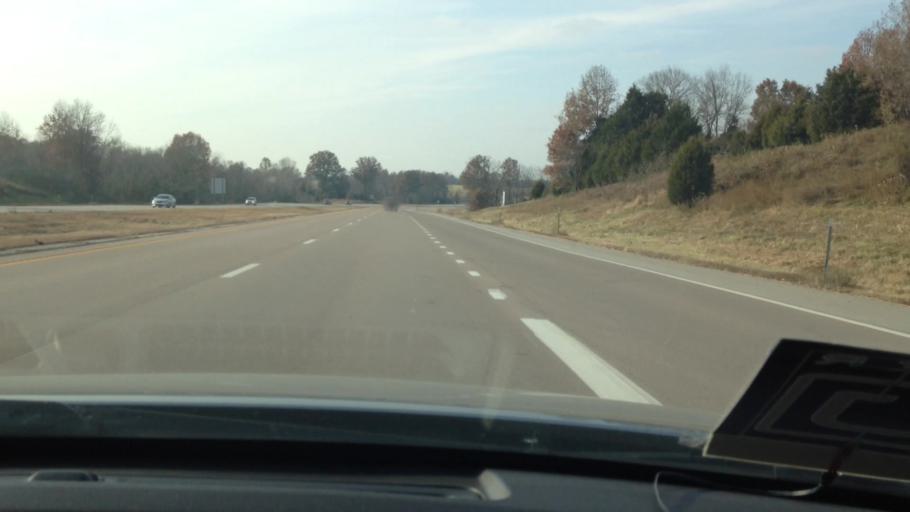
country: US
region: Missouri
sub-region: Cass County
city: Garden City
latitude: 38.4681
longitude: -94.0066
